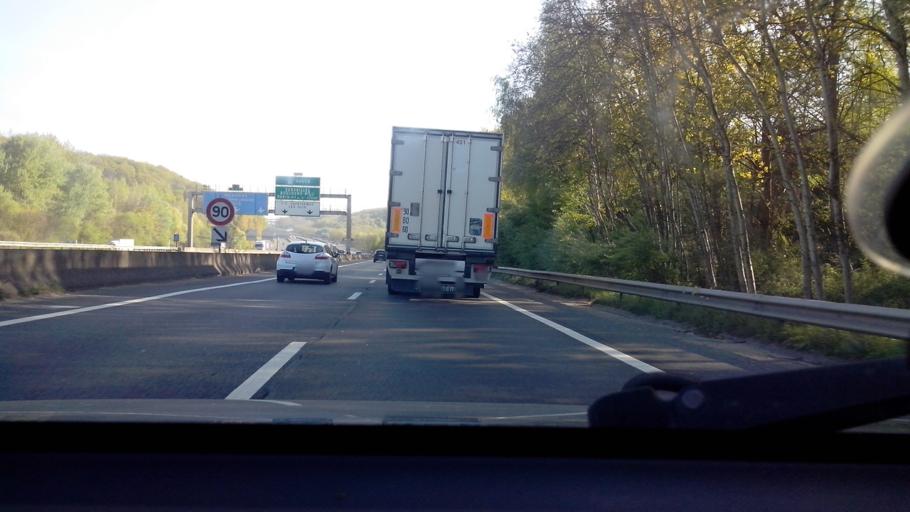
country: FR
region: Ile-de-France
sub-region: Departement de l'Essonne
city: Les Ulis
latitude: 48.6568
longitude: 2.1815
